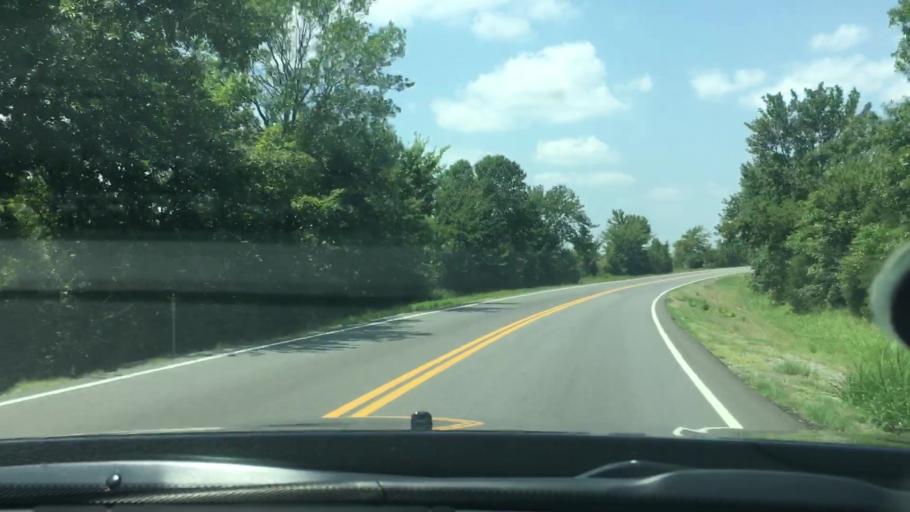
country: US
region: Oklahoma
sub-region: Atoka County
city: Atoka
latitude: 34.3752
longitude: -96.2591
